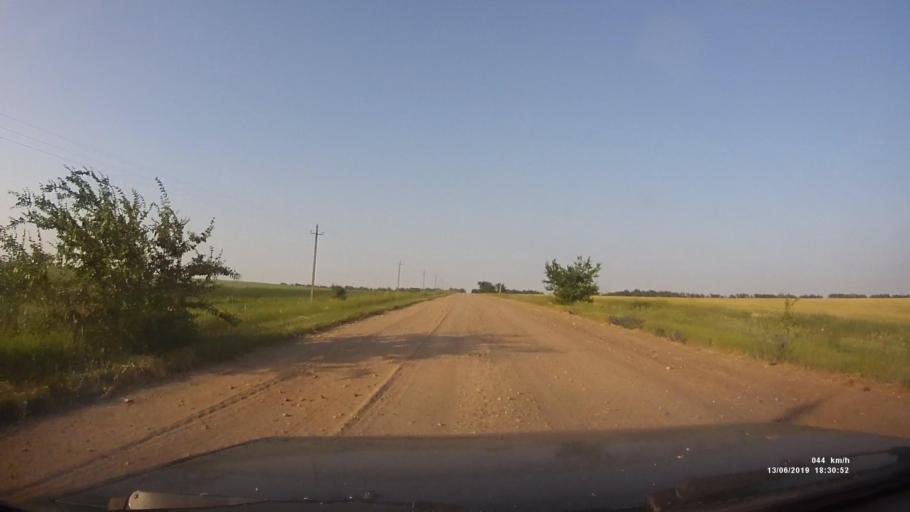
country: RU
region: Rostov
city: Kazanskaya
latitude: 49.8639
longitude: 41.3536
